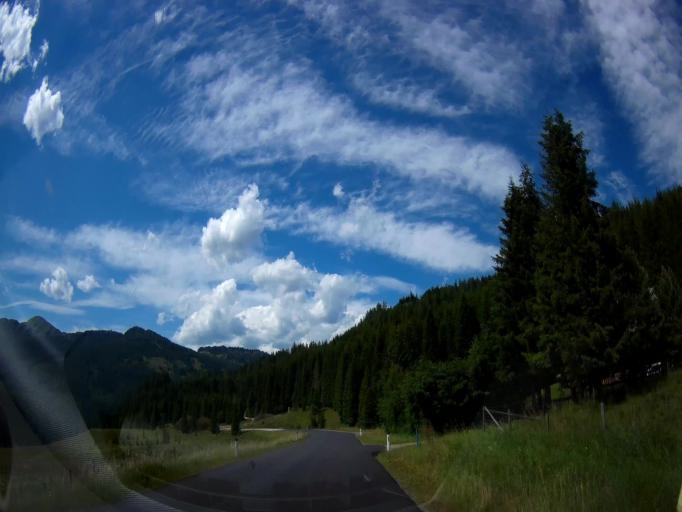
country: AT
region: Styria
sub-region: Politischer Bezirk Murau
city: Stadl an der Mur
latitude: 46.9701
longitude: 14.0166
